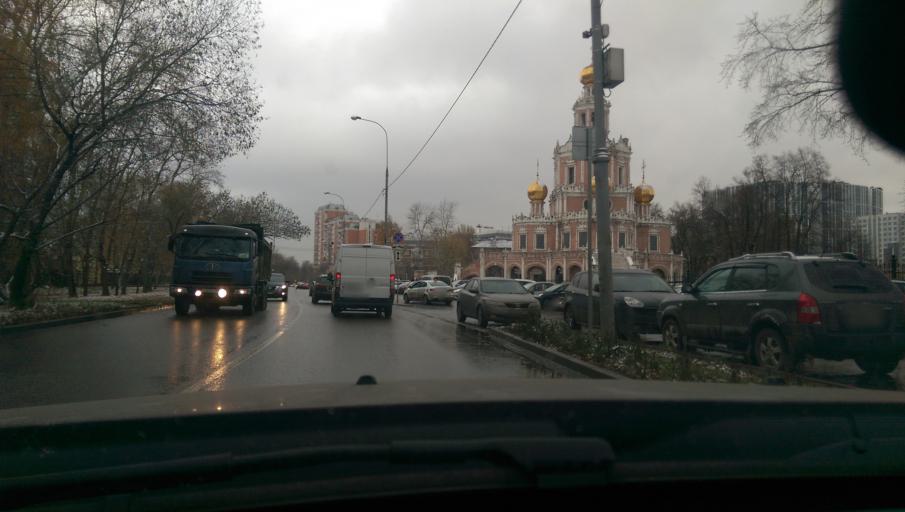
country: RU
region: Moskovskaya
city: Fili
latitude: 55.7498
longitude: 37.5109
